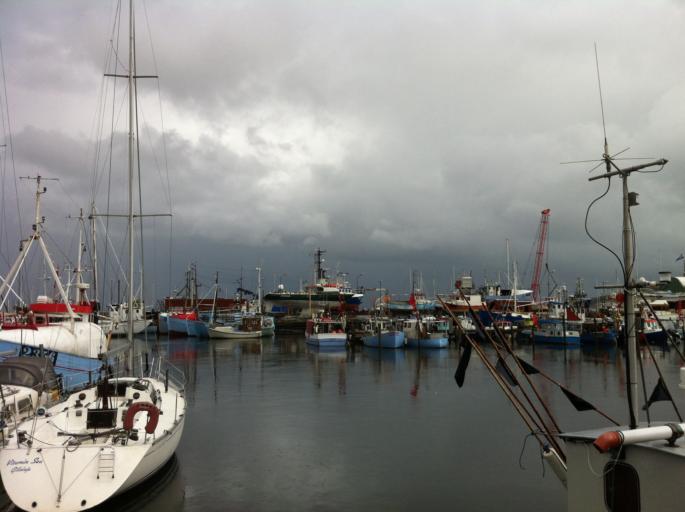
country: DK
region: Capital Region
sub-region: Gribskov Kommune
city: Gilleleje
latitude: 56.1261
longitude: 12.3088
